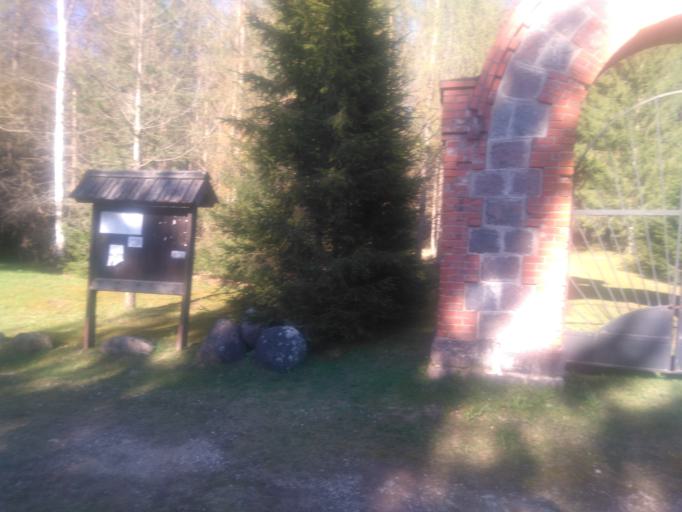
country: LV
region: Vecpiebalga
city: Vecpiebalga
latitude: 57.0108
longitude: 25.8404
